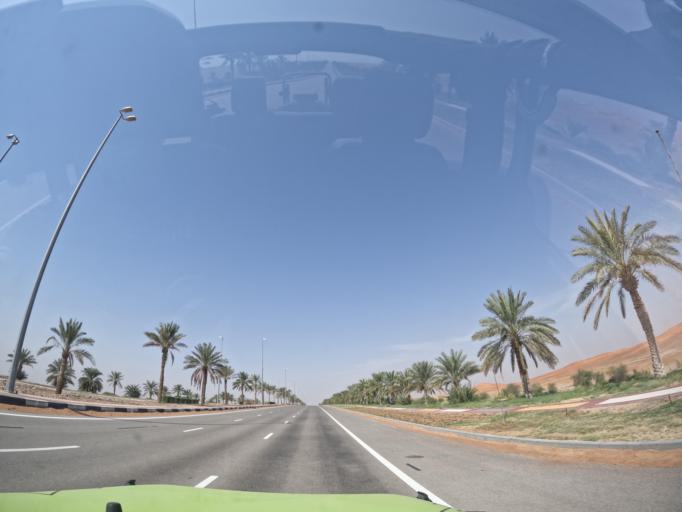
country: AE
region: Abu Dhabi
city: Al Ain
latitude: 24.2597
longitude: 55.6454
